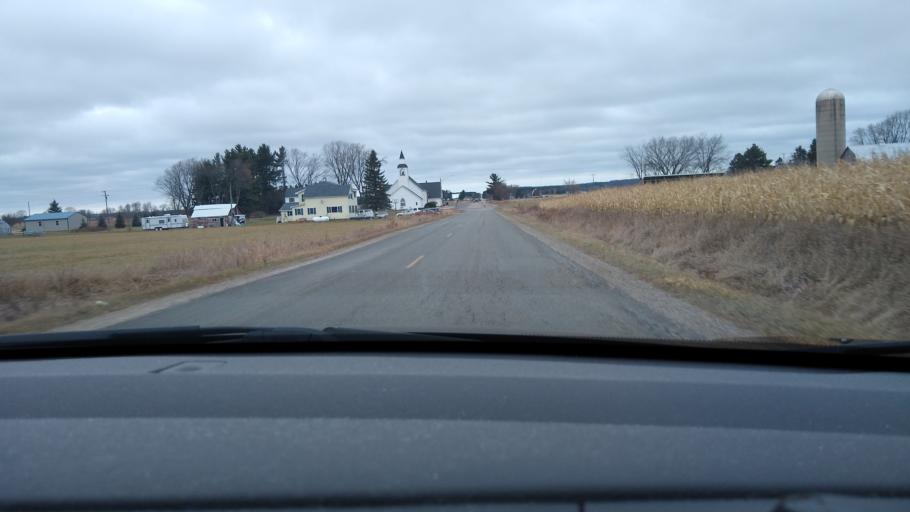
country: US
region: Michigan
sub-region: Missaukee County
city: Lake City
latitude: 44.2413
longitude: -85.0534
